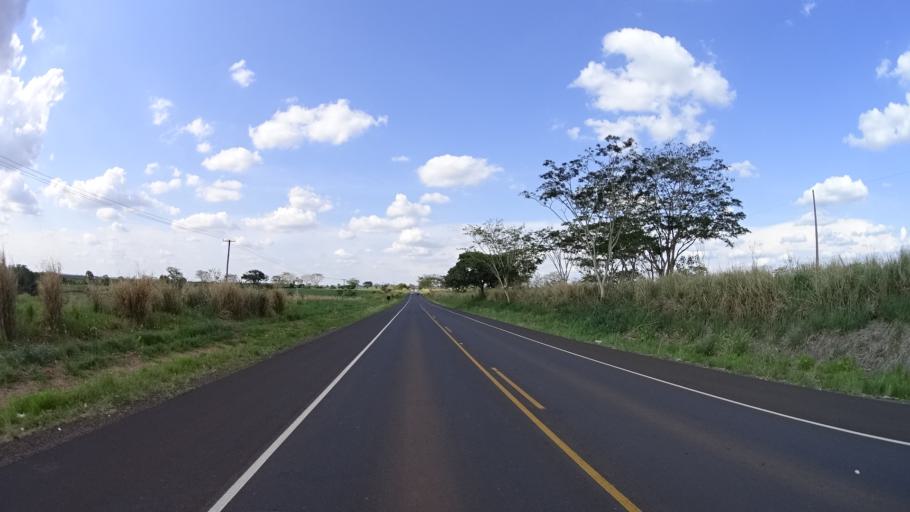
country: BR
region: Sao Paulo
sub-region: Urupes
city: Urupes
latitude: -21.0270
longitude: -49.2354
